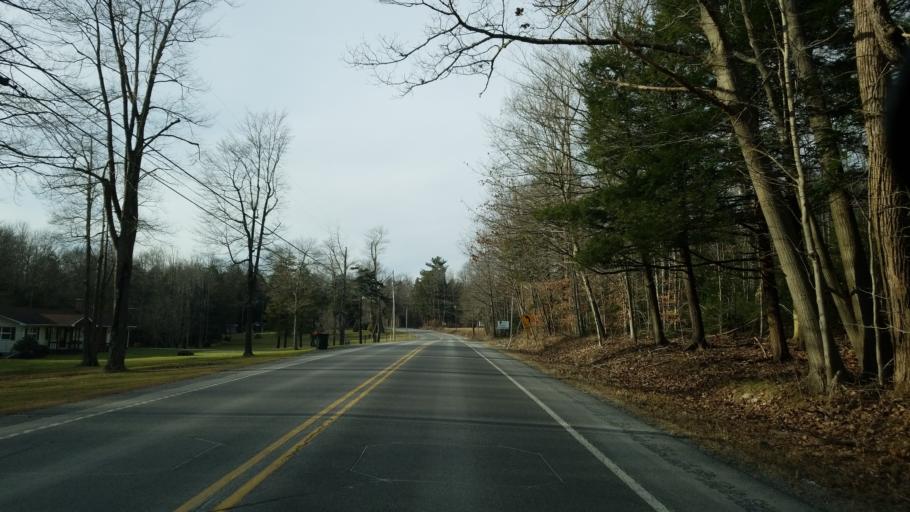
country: US
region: Pennsylvania
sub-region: Clearfield County
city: DuBois
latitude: 41.0288
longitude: -78.6752
